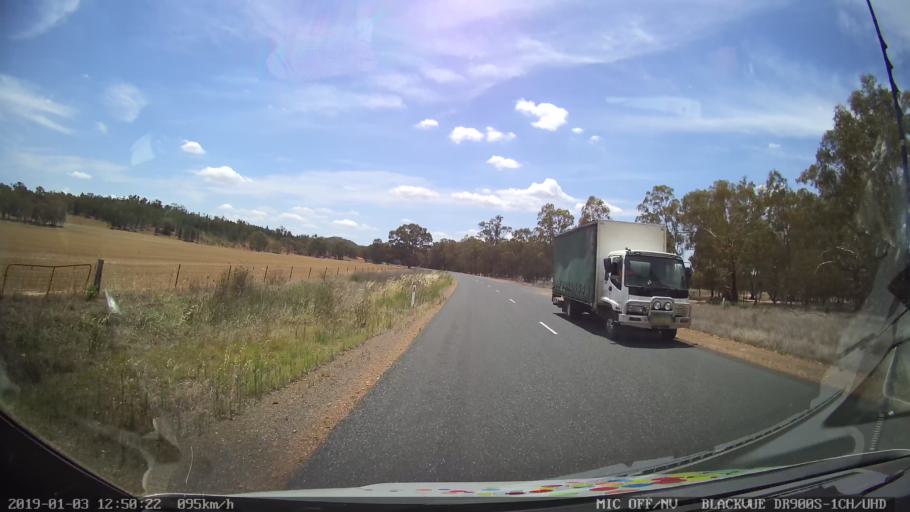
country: AU
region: New South Wales
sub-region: Weddin
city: Grenfell
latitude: -33.6923
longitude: 148.2697
